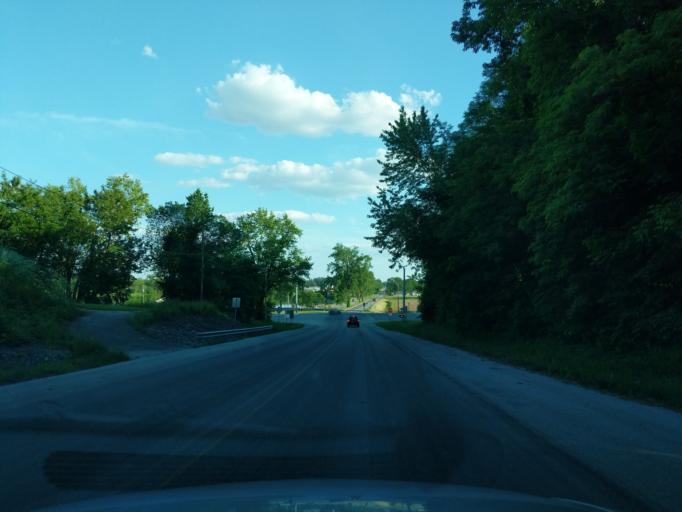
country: US
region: Indiana
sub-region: Huntington County
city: Huntington
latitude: 40.8971
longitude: -85.4715
